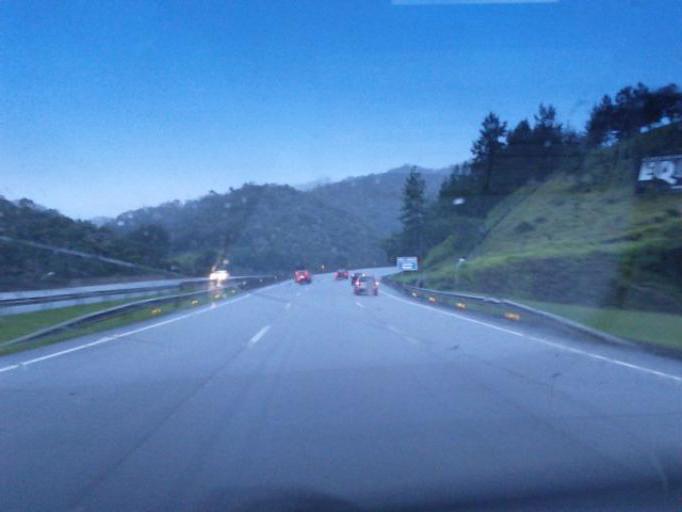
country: BR
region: Sao Paulo
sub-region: Juquitiba
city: Juquitiba
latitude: -24.0052
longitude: -47.1586
